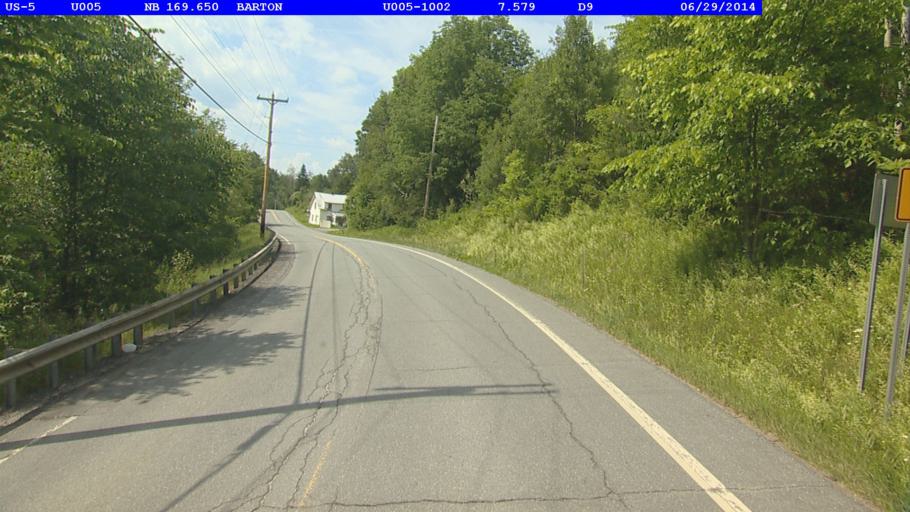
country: US
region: Vermont
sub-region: Orleans County
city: Newport
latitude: 44.7681
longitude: -72.2058
